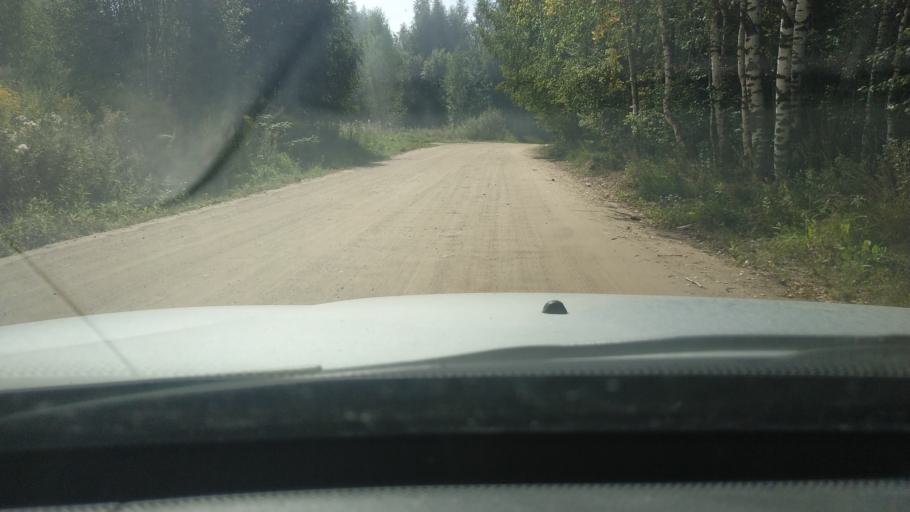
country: RU
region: Kostroma
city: Kosmynino
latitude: 57.7711
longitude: 40.7302
